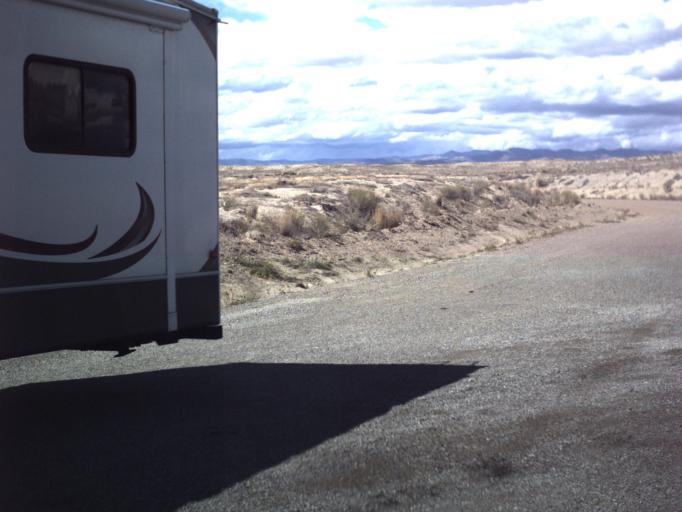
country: US
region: Colorado
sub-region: Mesa County
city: Loma
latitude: 39.1153
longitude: -109.1857
